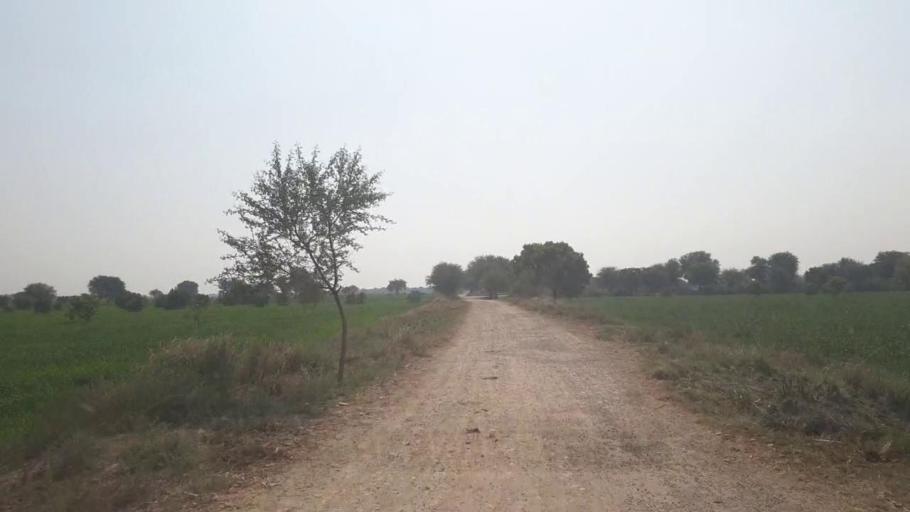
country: PK
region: Sindh
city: Tando Allahyar
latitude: 25.4772
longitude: 68.8350
